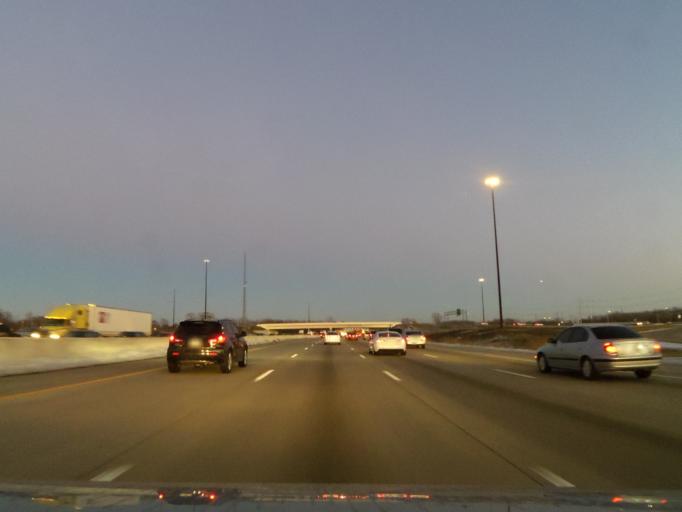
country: US
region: Indiana
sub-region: Lake County
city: Gary
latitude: 41.5688
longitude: -87.3601
